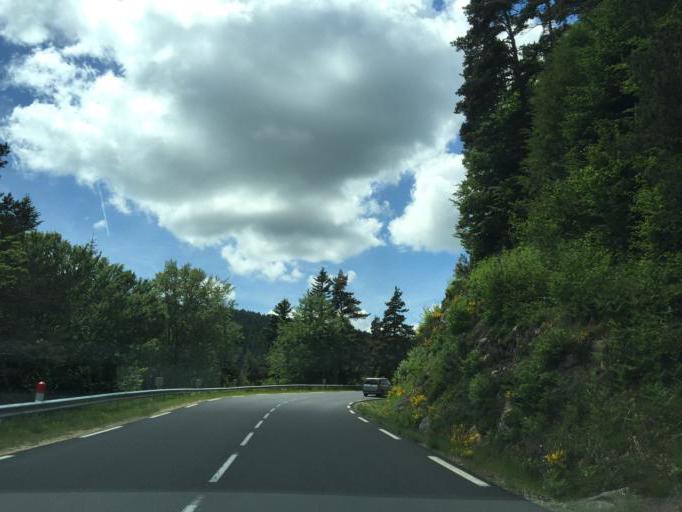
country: FR
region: Rhone-Alpes
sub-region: Departement de la Loire
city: Usson-en-Forez
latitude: 45.5166
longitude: 3.8858
